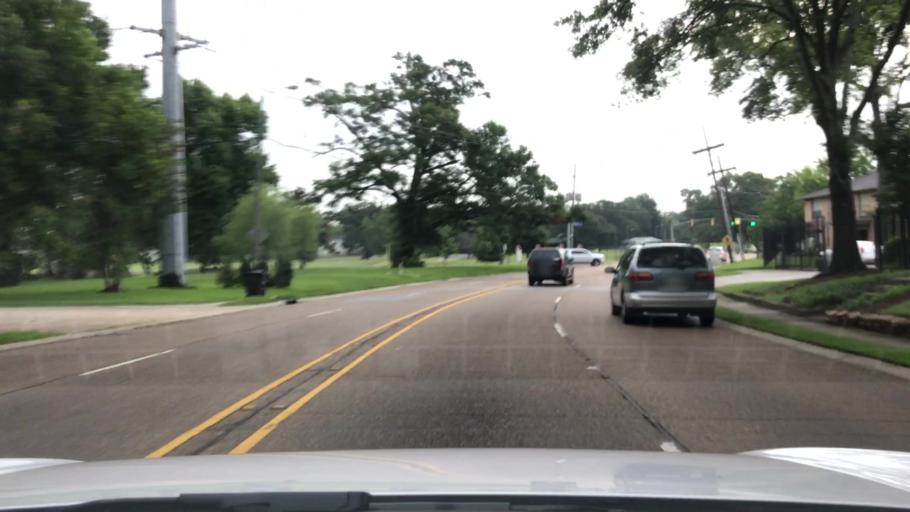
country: US
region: Louisiana
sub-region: East Baton Rouge Parish
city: Baton Rouge
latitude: 30.4345
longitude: -91.1345
